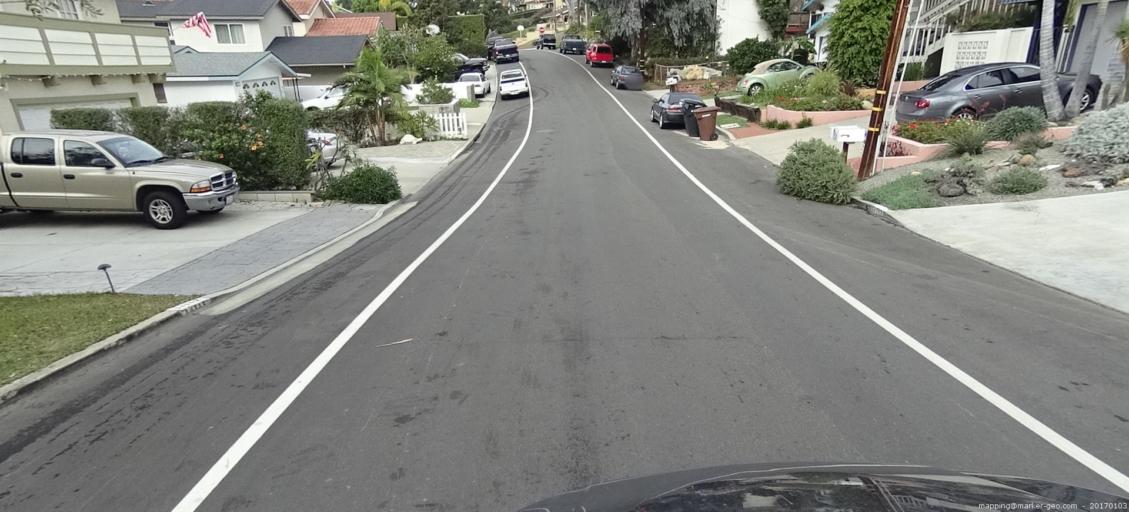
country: US
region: California
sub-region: Orange County
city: San Juan Capistrano
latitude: 33.4630
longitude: -117.6584
